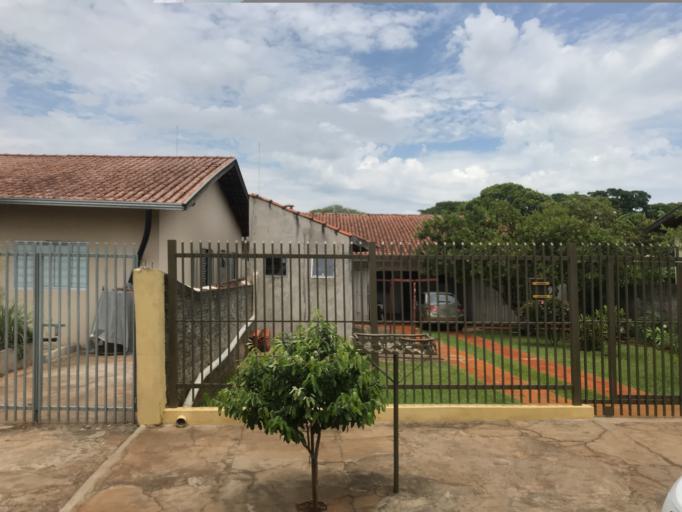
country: BR
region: Parana
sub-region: Londrina
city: Londrina
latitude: -23.2898
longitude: -51.2071
